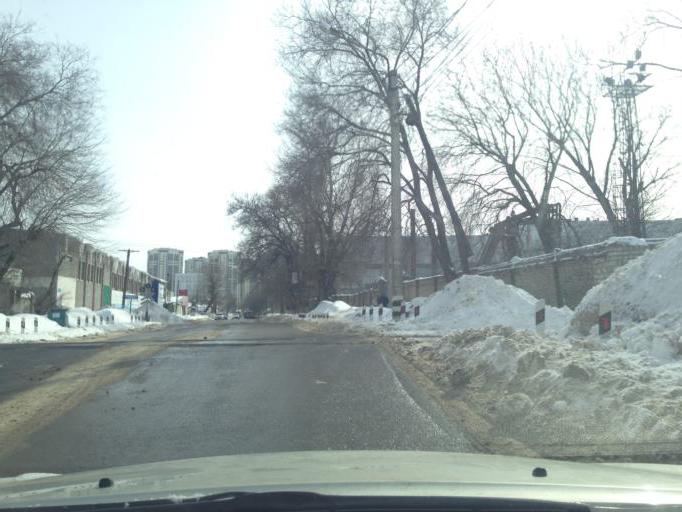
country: RU
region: Voronezj
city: Voronezh
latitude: 51.6609
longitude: 39.1734
